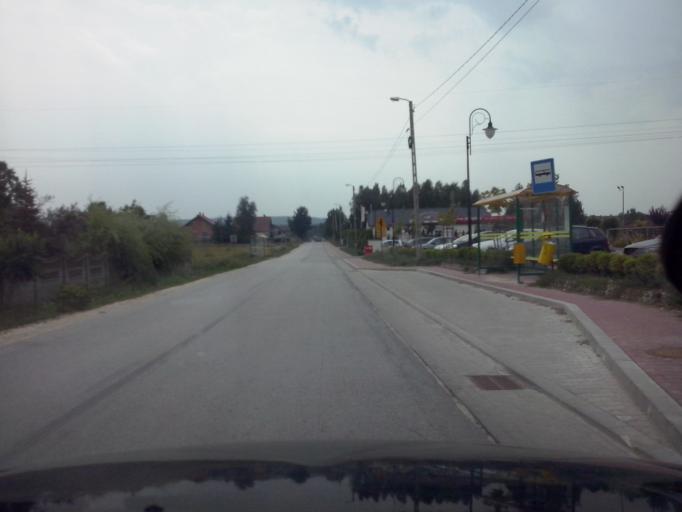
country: PL
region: Swietokrzyskie
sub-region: Powiat kielecki
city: Brzeziny
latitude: 50.7605
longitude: 20.5951
